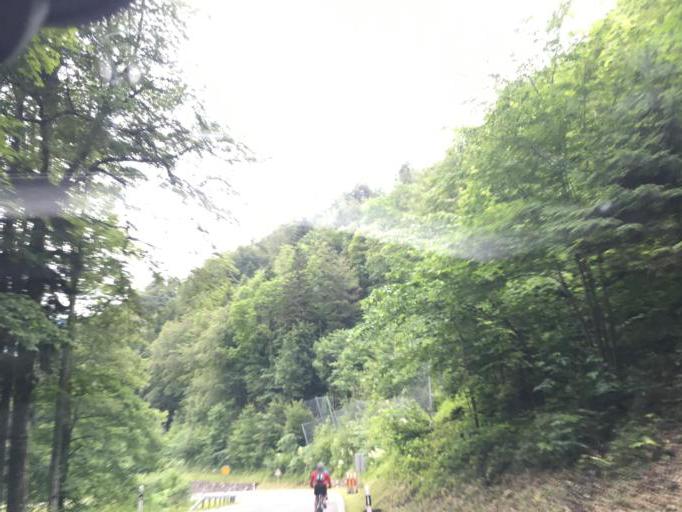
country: CH
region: Obwalden
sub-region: Obwalden
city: Engelberg
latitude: 46.8452
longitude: 8.3759
